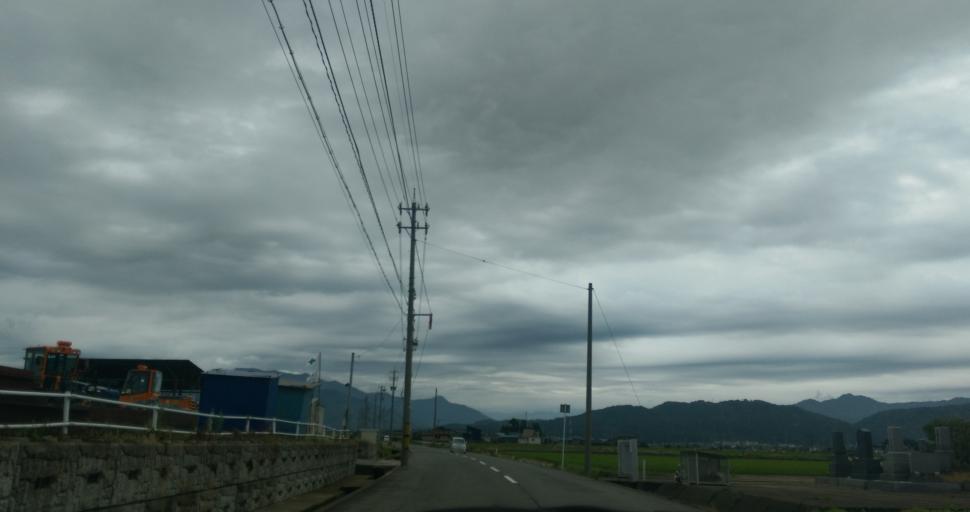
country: JP
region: Fukui
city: Fukui-shi
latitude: 36.0982
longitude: 136.2599
